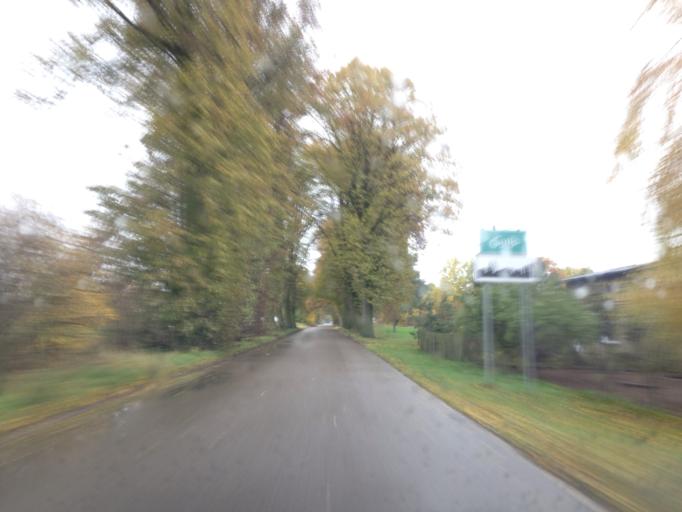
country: PL
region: Warmian-Masurian Voivodeship
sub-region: Powiat nowomiejski
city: Biskupiec
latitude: 53.5840
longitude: 19.4250
